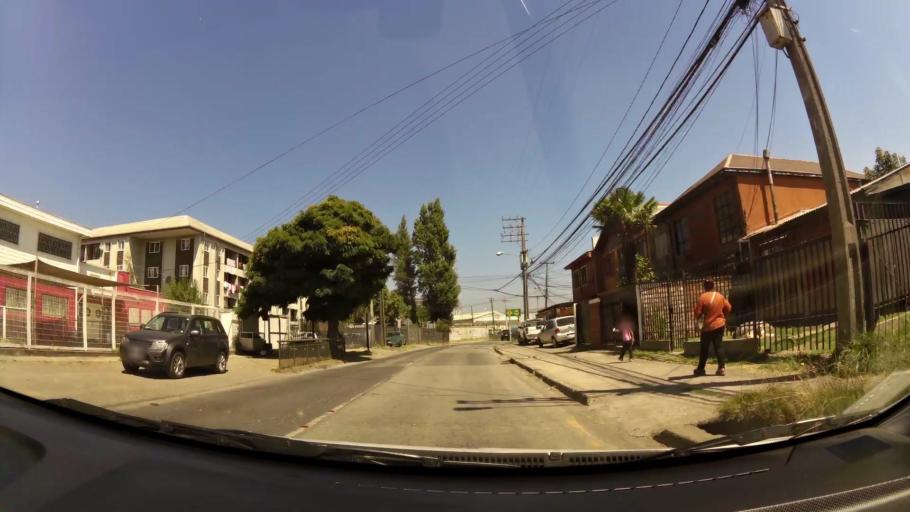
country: CL
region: Biobio
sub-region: Provincia de Concepcion
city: Concepcion
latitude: -36.8102
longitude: -73.0594
